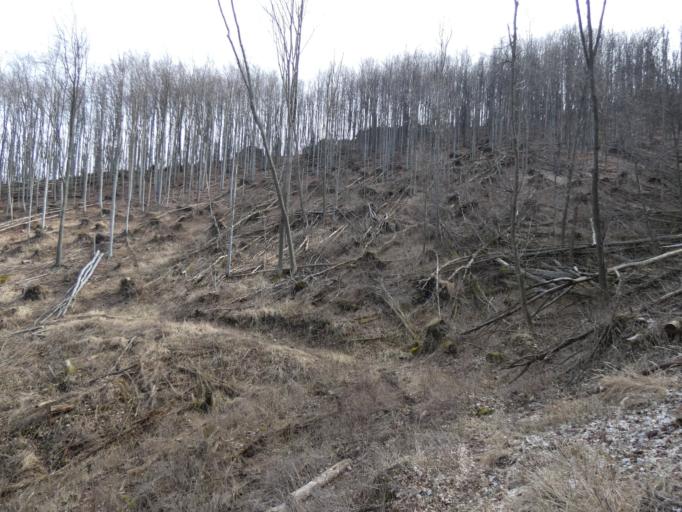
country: HU
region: Nograd
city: Diosjeno
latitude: 47.9612
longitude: 18.9415
